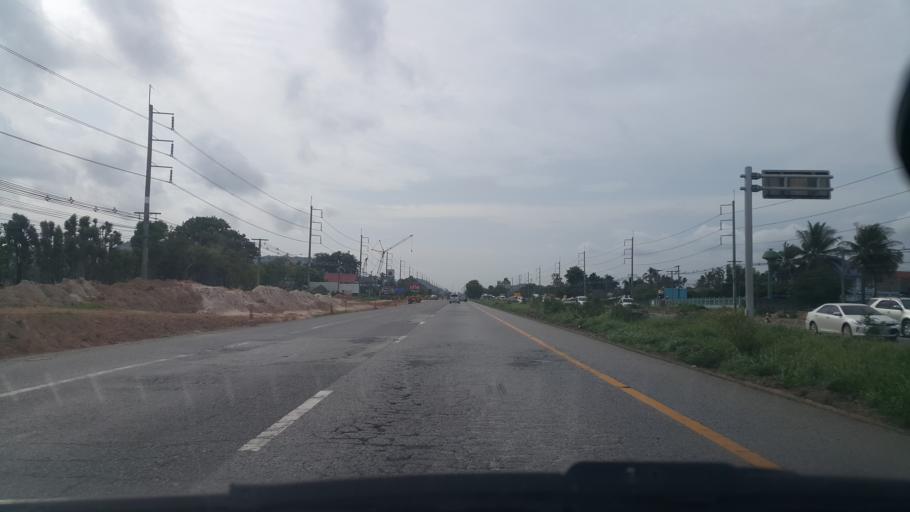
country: TH
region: Rayong
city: Nikhom Phattana
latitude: 12.7999
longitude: 101.1486
